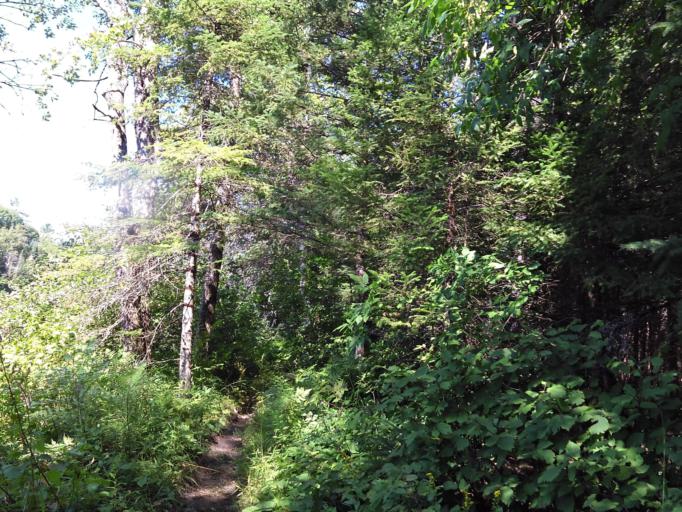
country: CA
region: Ontario
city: Renfrew
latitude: 45.2537
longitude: -77.1934
